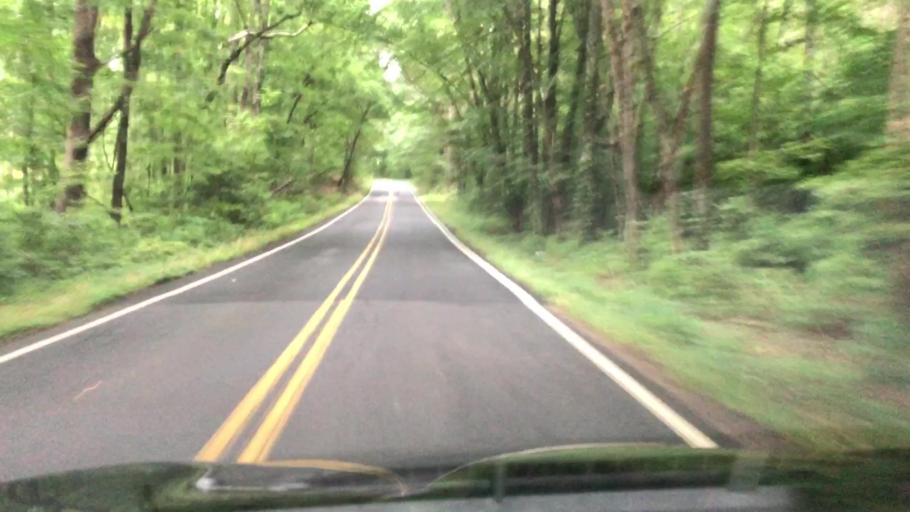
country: US
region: Virginia
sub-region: Fauquier County
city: Bealeton
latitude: 38.4961
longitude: -77.6007
